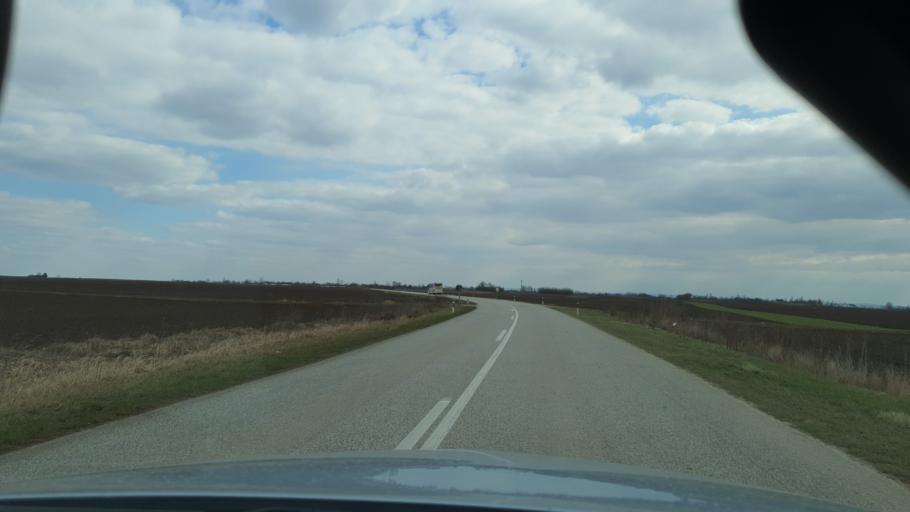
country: RS
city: Obrovac
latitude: 45.4259
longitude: 19.3879
